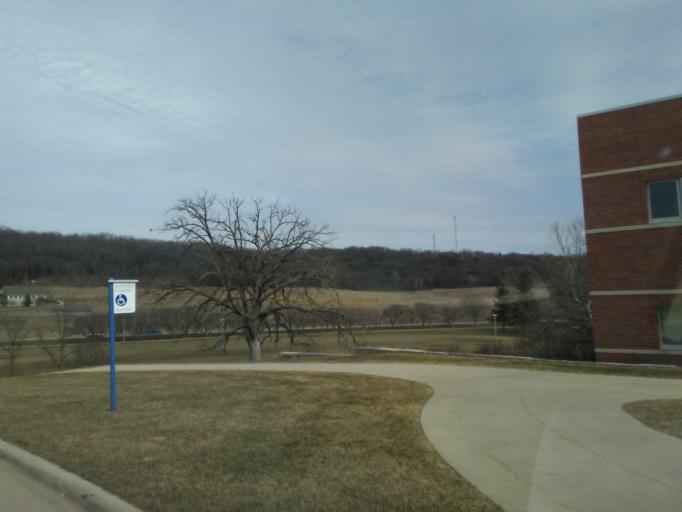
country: US
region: Iowa
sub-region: Winneshiek County
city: Decorah
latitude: 43.3142
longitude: -91.8039
